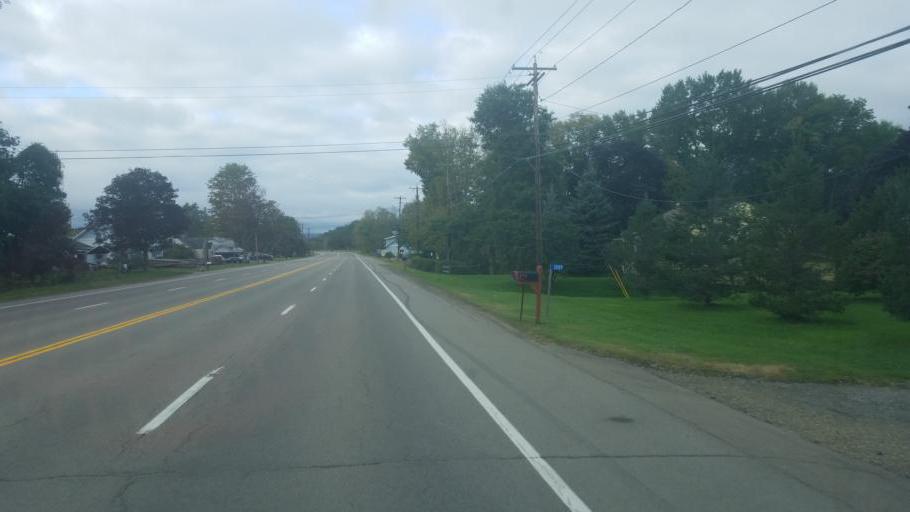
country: US
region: New York
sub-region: Cattaraugus County
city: Olean
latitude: 42.1340
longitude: -78.4055
